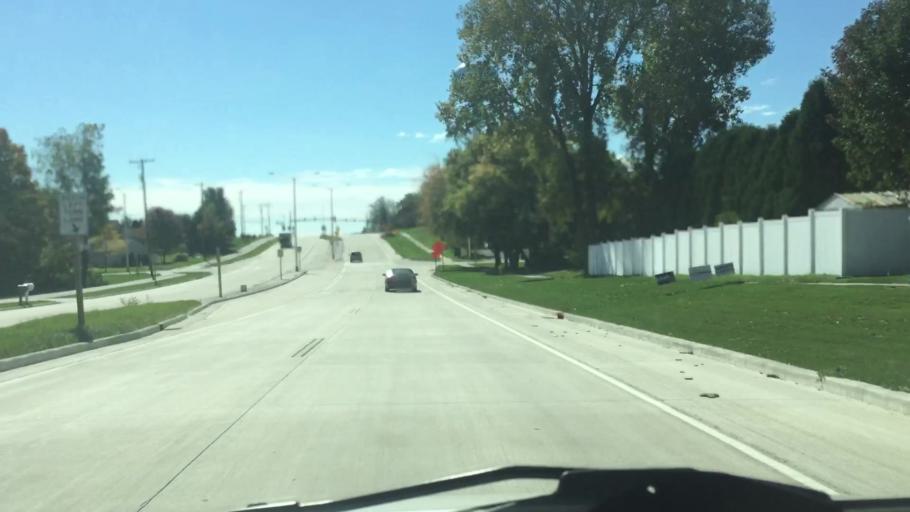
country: US
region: Wisconsin
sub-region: Waukesha County
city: Pewaukee
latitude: 43.0398
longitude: -88.2860
